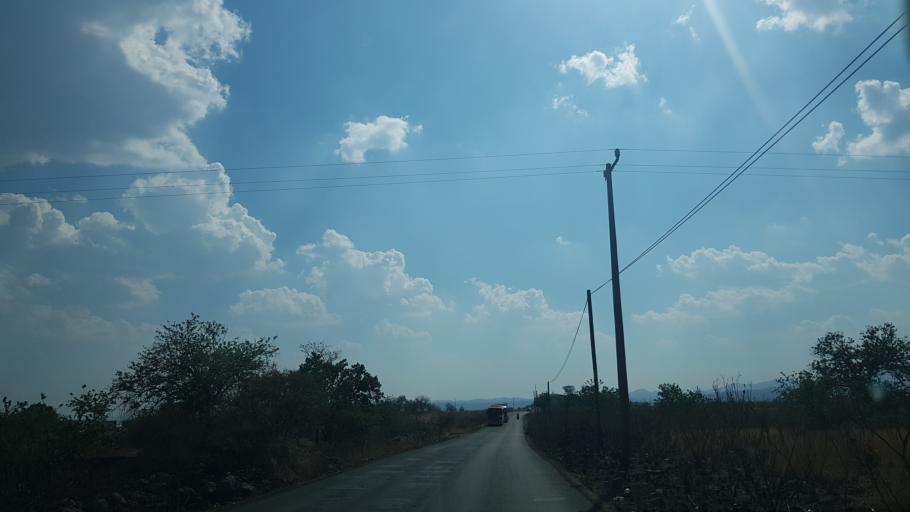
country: MX
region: Puebla
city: Atlixco
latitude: 18.9027
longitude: -98.4865
